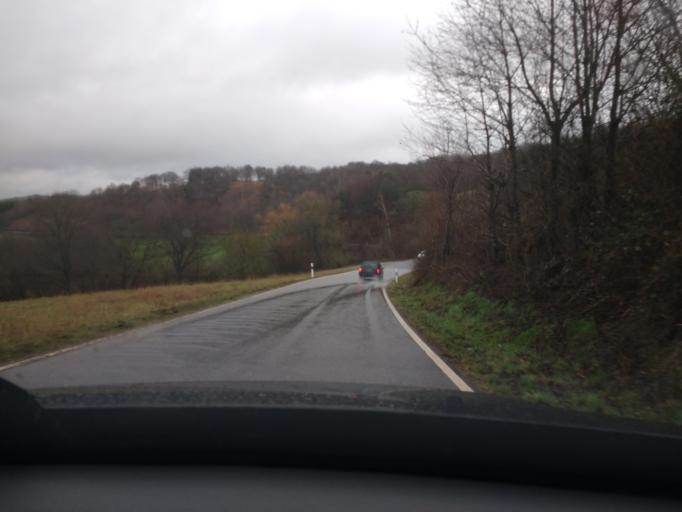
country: DE
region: Rheinland-Pfalz
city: Hockweiler
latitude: 49.7134
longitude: 6.6941
